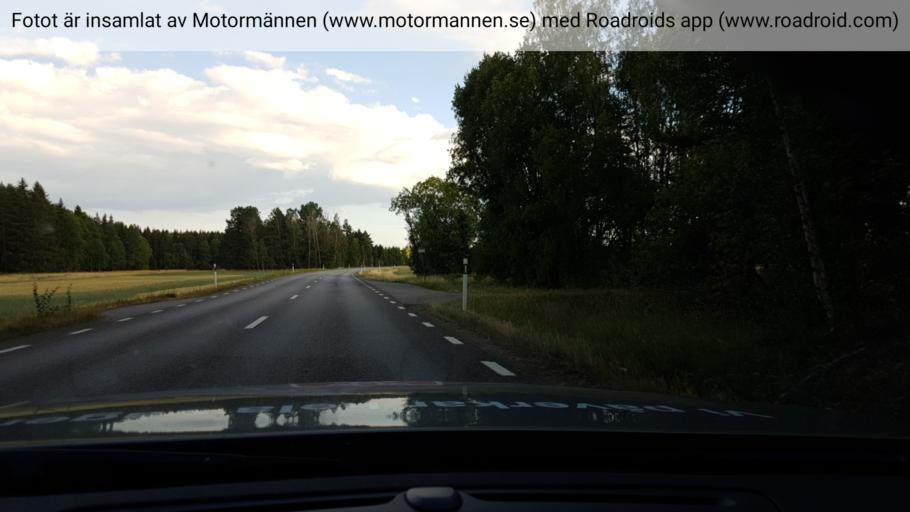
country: SE
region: Uppsala
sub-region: Enkopings Kommun
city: Irsta
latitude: 59.7868
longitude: 16.9049
